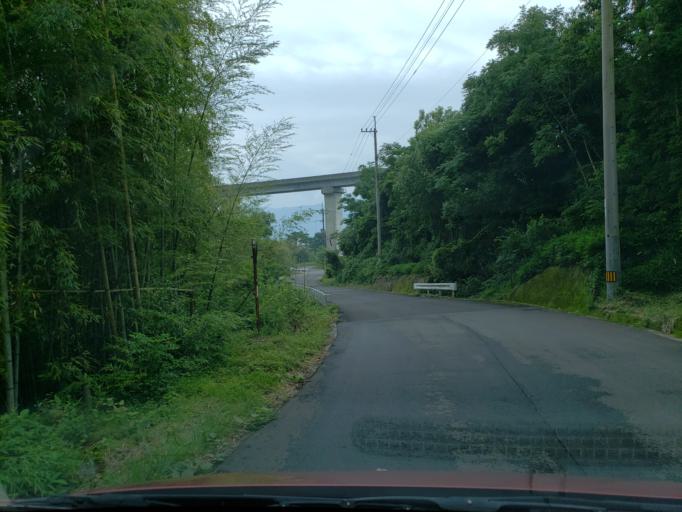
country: JP
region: Tokushima
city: Kamojimacho-jogejima
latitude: 34.1057
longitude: 134.2978
